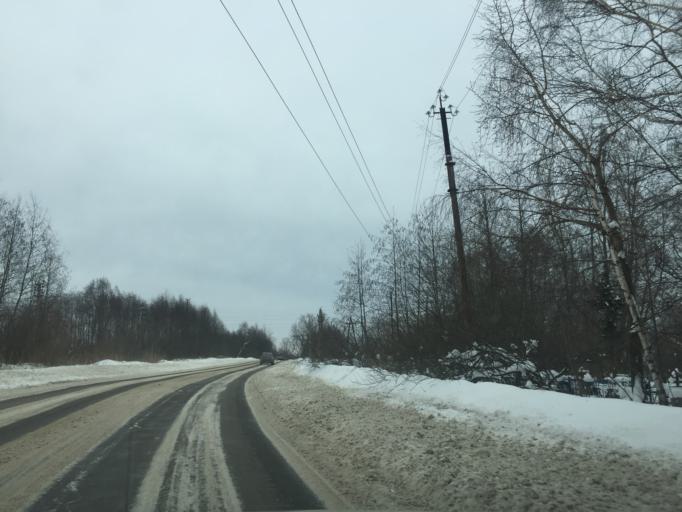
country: RU
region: Leningrad
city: Imeni Sverdlova
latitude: 59.7915
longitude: 30.6891
